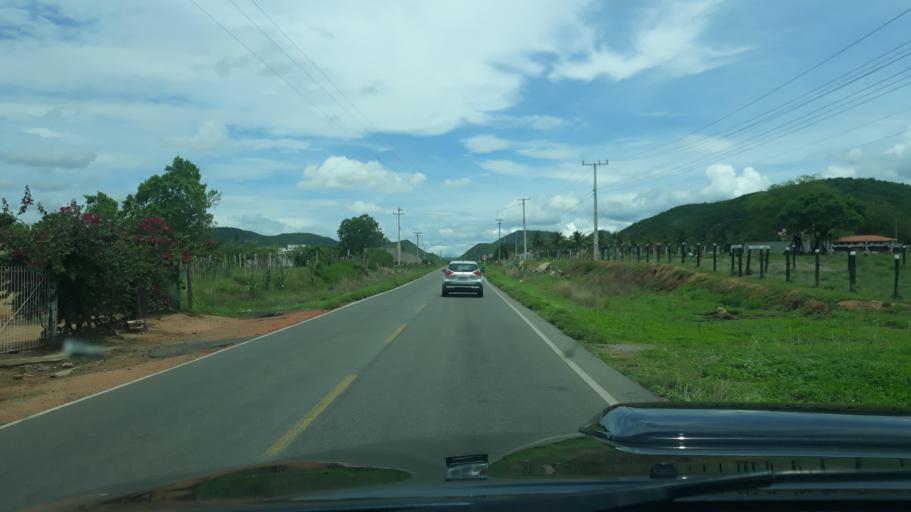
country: BR
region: Bahia
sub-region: Guanambi
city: Guanambi
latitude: -14.2540
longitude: -42.7396
